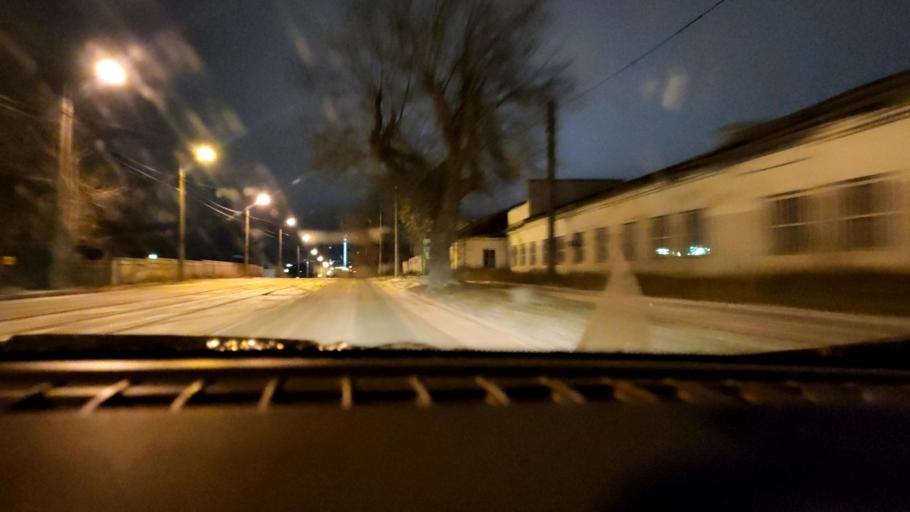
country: RU
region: Perm
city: Kondratovo
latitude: 58.0078
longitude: 56.1741
